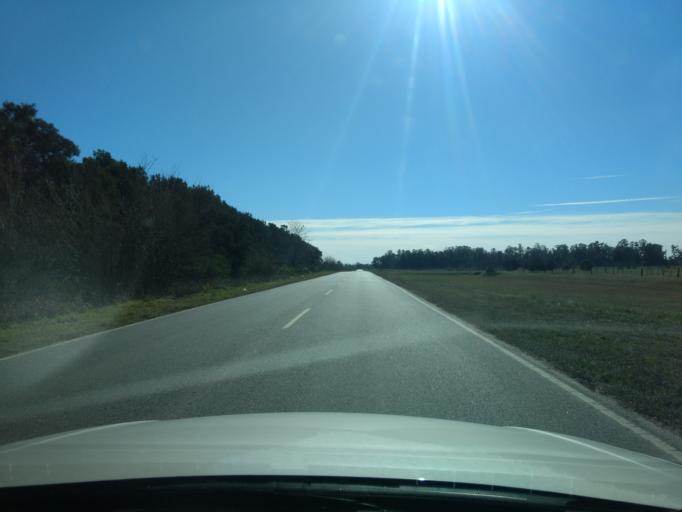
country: AR
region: Buenos Aires
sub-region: Partido de Lujan
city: Lujan
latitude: -34.6126
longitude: -59.1063
